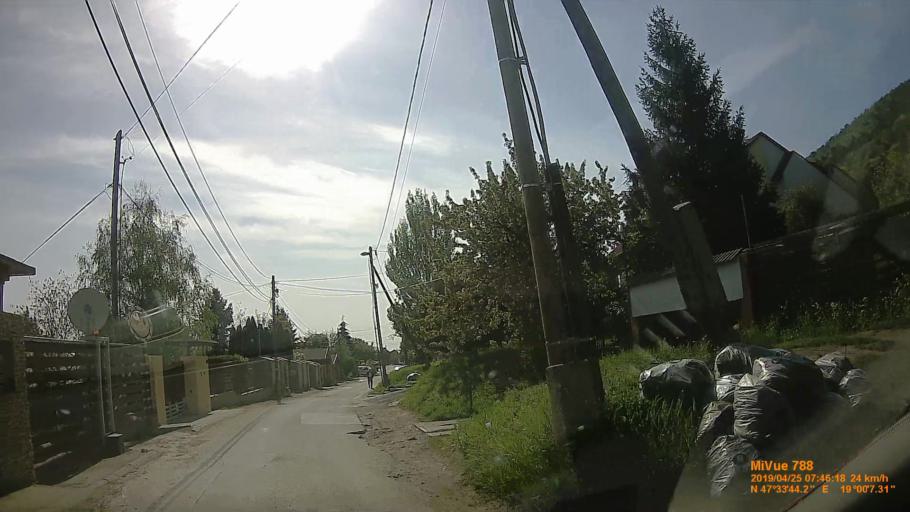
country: HU
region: Pest
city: Urom
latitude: 47.5623
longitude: 19.0021
